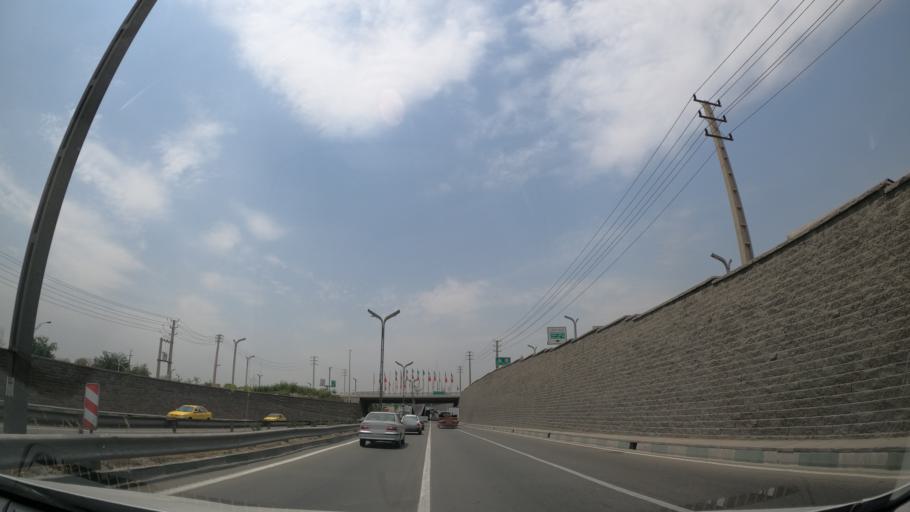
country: IR
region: Tehran
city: Shahr-e Qods
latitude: 35.7028
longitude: 51.1852
